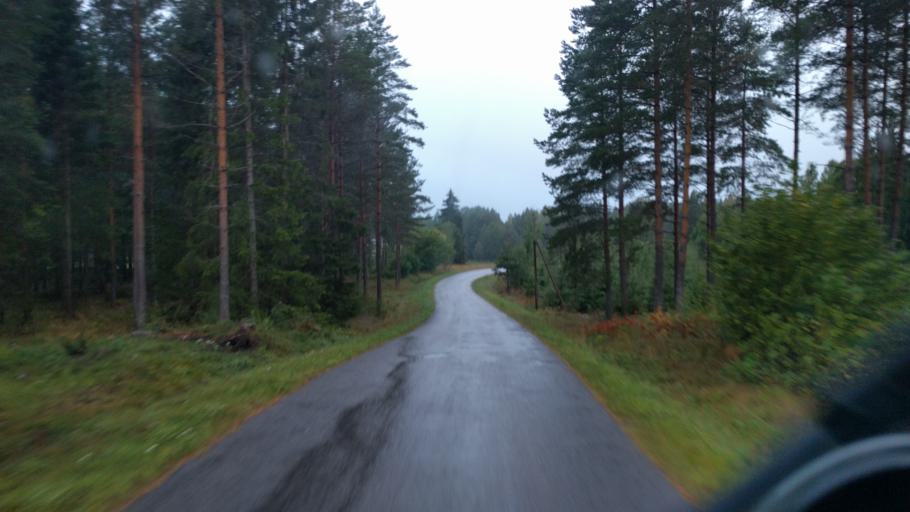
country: SE
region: Kalmar
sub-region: Vasterviks Kommun
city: Ankarsrum
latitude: 57.8244
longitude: 16.2979
